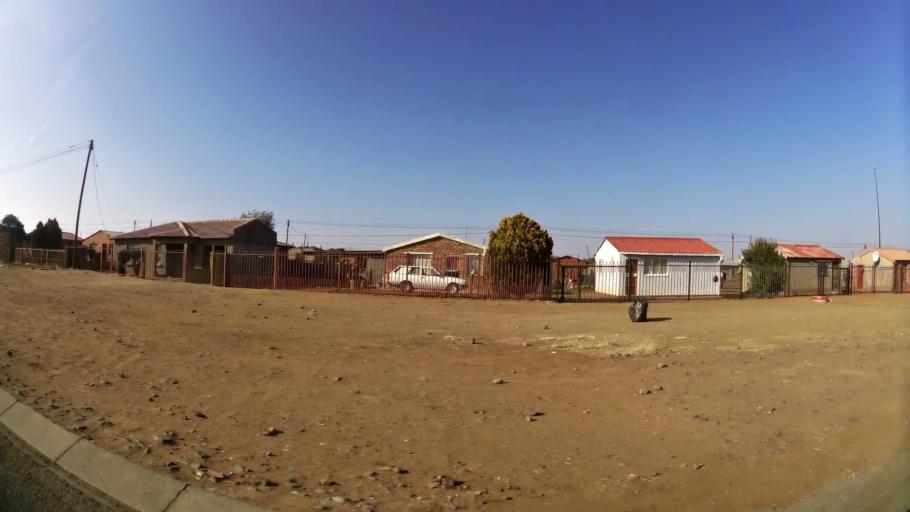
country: ZA
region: Orange Free State
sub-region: Mangaung Metropolitan Municipality
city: Bloemfontein
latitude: -29.2011
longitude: 26.2216
